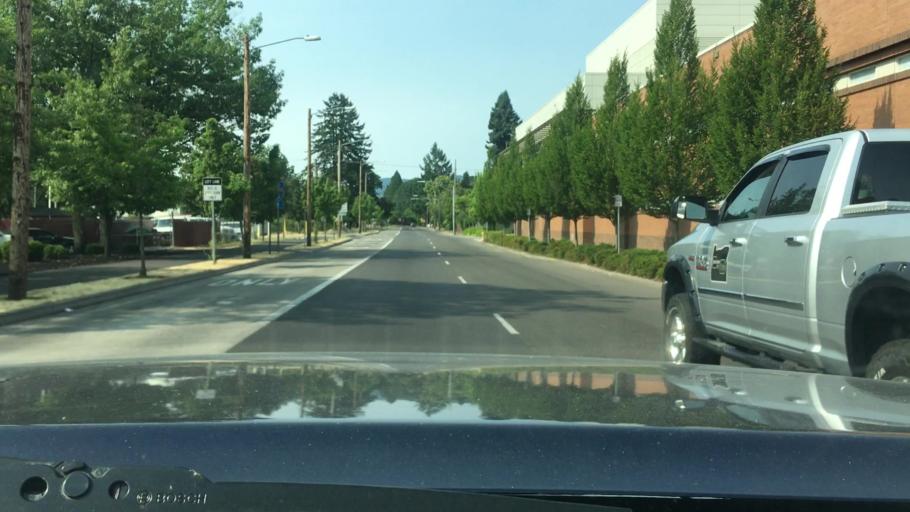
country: US
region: Oregon
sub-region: Lane County
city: Springfield
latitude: 44.0471
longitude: -123.0221
